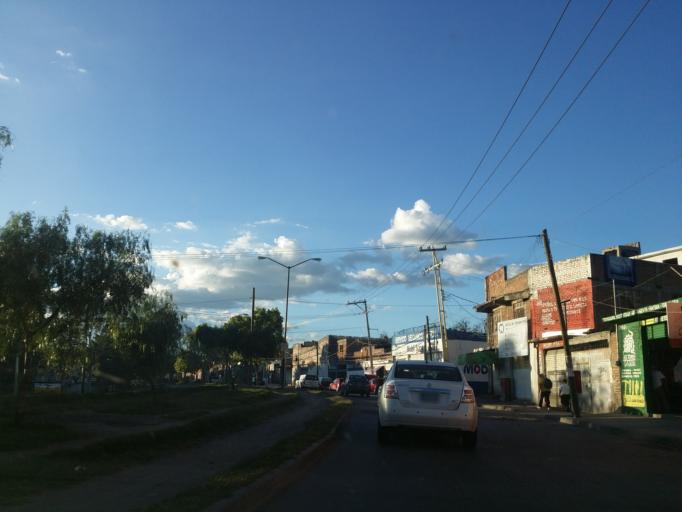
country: MX
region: Guanajuato
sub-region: Leon
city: Medina
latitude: 21.1963
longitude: -101.6675
